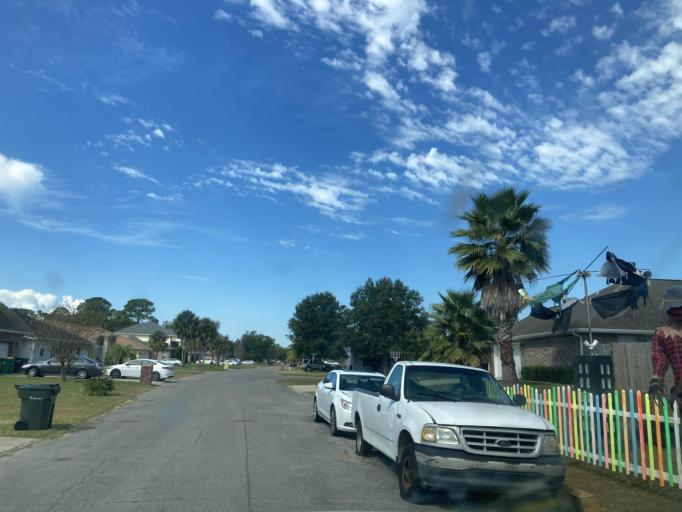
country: US
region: Mississippi
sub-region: Jackson County
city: Saint Martin
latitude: 30.4367
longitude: -88.8553
